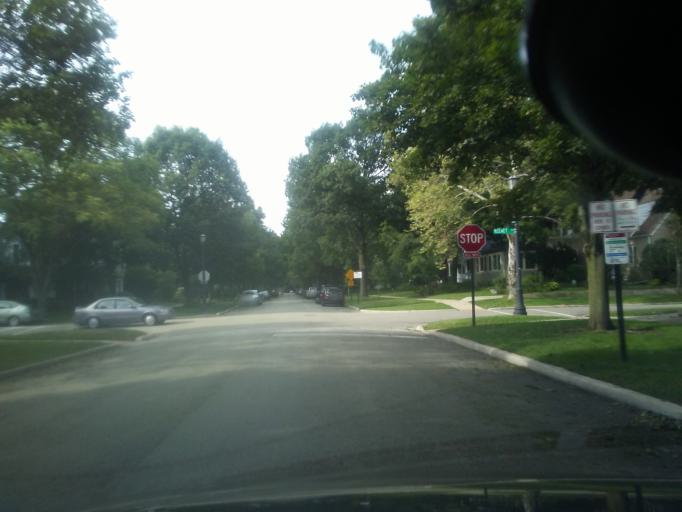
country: US
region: Illinois
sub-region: Cook County
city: Evanston
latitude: 42.0291
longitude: -87.6736
